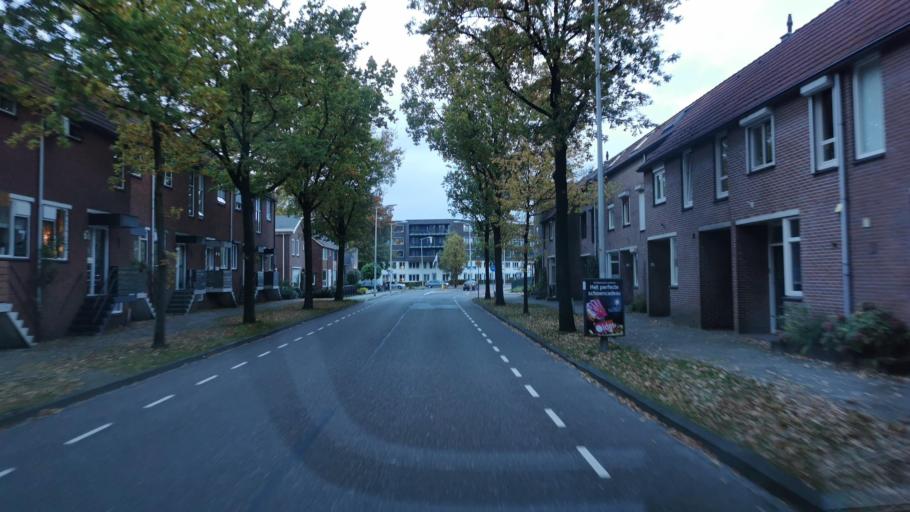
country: NL
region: Overijssel
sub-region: Gemeente Oldenzaal
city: Oldenzaal
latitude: 52.3136
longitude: 6.9337
